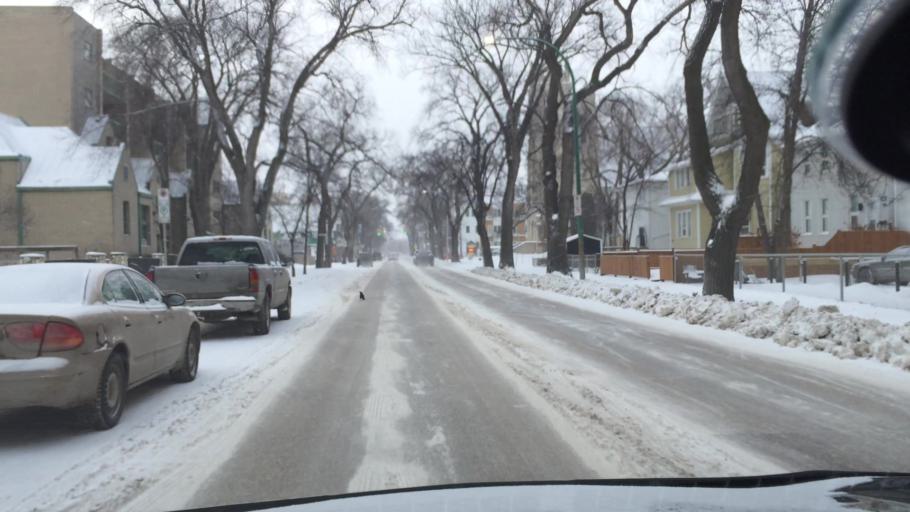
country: CA
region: Manitoba
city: Winnipeg
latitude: 49.8834
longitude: -97.1609
